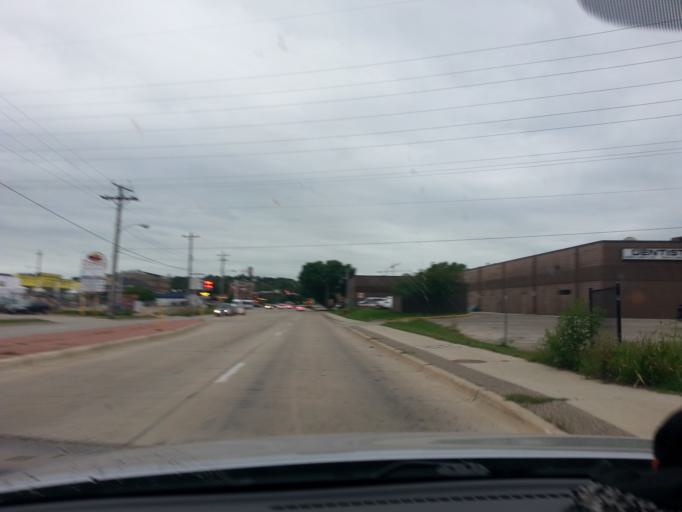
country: US
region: Minnesota
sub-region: Olmsted County
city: Rochester
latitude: 44.0304
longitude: -92.4791
